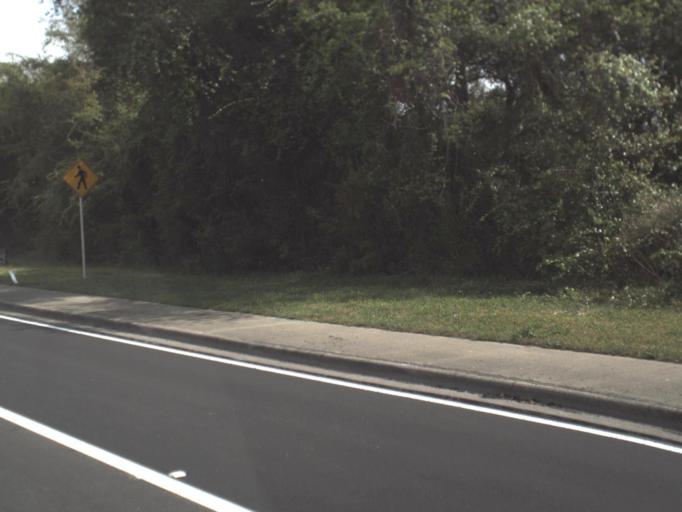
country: US
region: Florida
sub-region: Okaloosa County
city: Niceville
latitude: 30.4847
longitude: -86.4182
